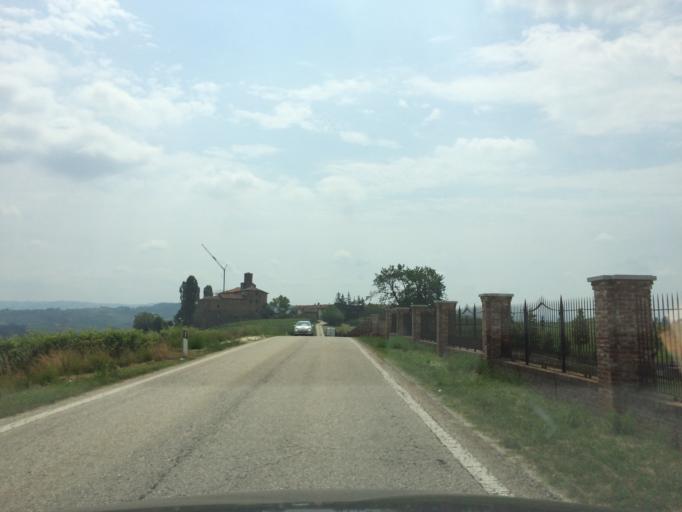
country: IT
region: Piedmont
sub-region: Provincia di Cuneo
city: Barolo
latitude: 44.6158
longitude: 7.9325
